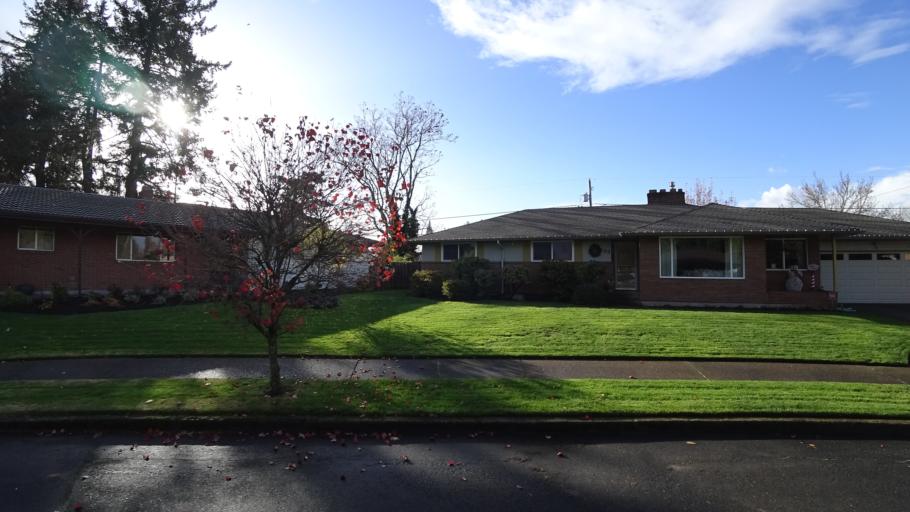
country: US
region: Oregon
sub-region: Multnomah County
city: Lents
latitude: 45.5270
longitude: -122.5506
